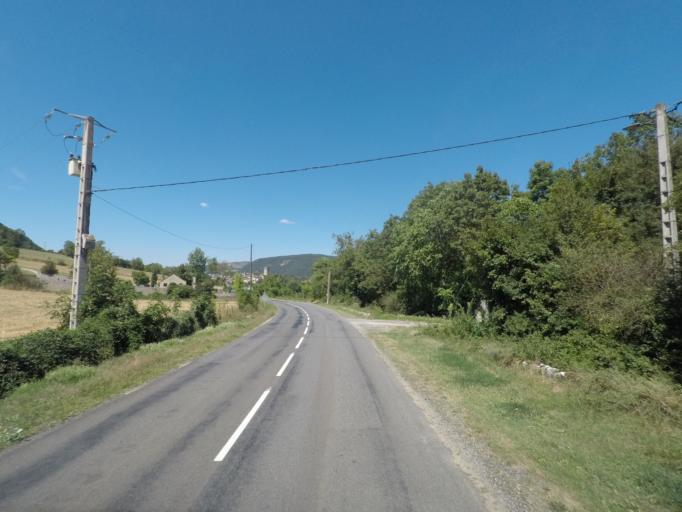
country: FR
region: Languedoc-Roussillon
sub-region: Departement de la Lozere
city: Chanac
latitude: 44.4606
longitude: 3.3505
